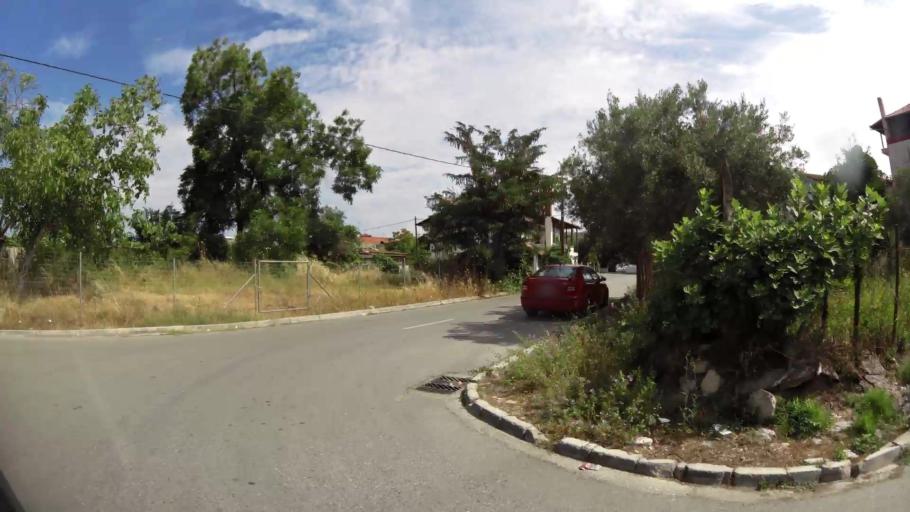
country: GR
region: Central Macedonia
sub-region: Nomos Pierias
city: Katerini
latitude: 40.2662
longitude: 22.4924
